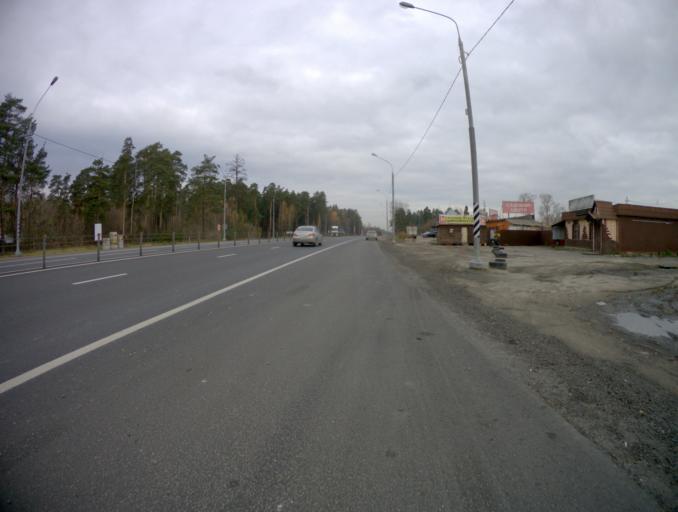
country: RU
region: Moskovskaya
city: Malaya Dubna
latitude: 55.8437
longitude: 38.9656
